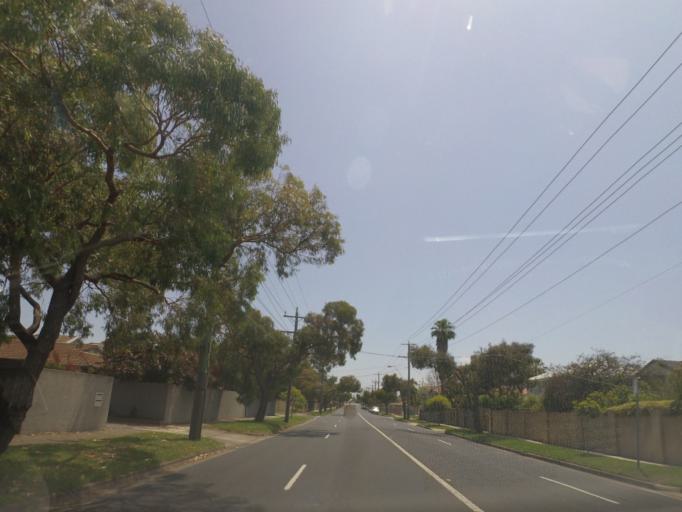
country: AU
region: Victoria
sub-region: Bayside
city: Hampton East
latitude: -37.9495
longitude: 145.0215
